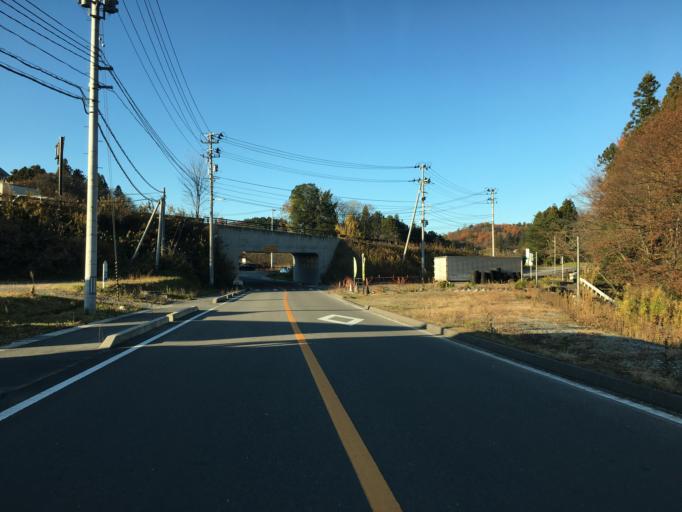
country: JP
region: Fukushima
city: Koriyama
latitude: 37.3707
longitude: 140.4443
